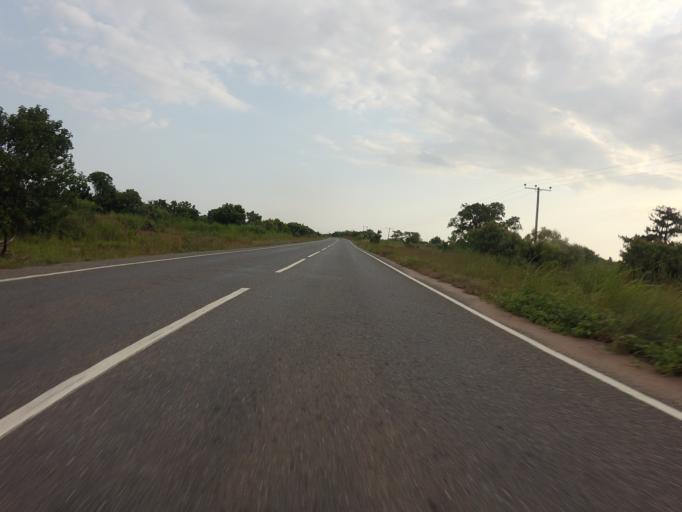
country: GH
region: Volta
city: Ho
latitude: 6.1107
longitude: 0.5166
